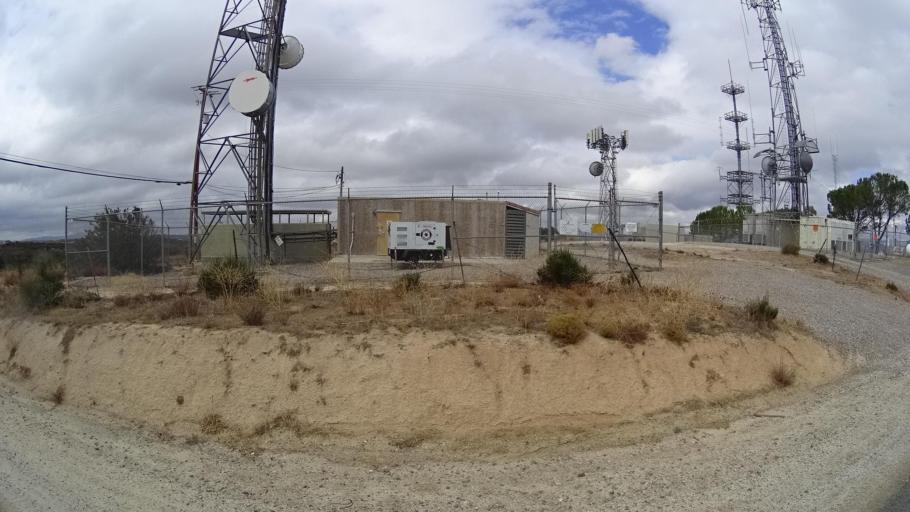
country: US
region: California
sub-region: San Diego County
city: Campo
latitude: 32.6468
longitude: -116.3173
